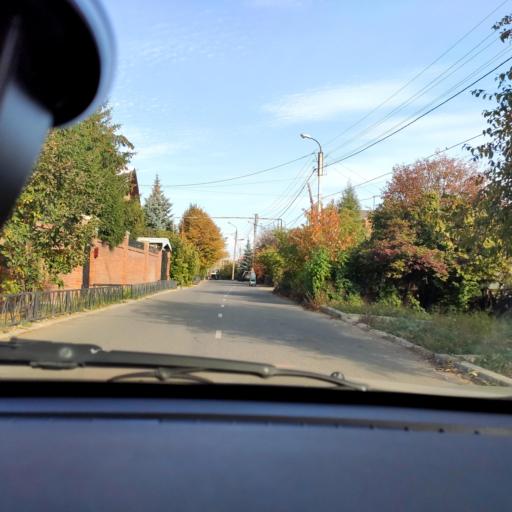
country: RU
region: Samara
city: Tol'yatti
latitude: 53.5339
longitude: 49.3884
